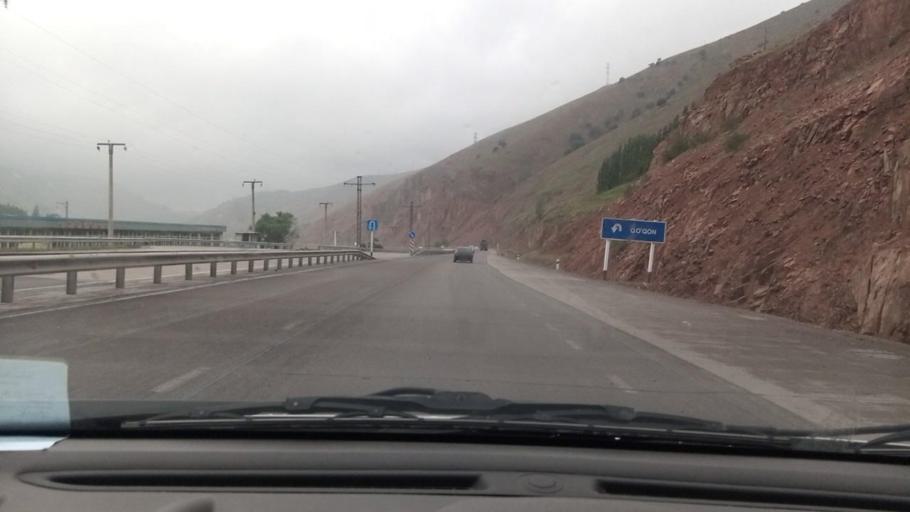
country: UZ
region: Toshkent
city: Angren
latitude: 41.1512
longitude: 70.4309
